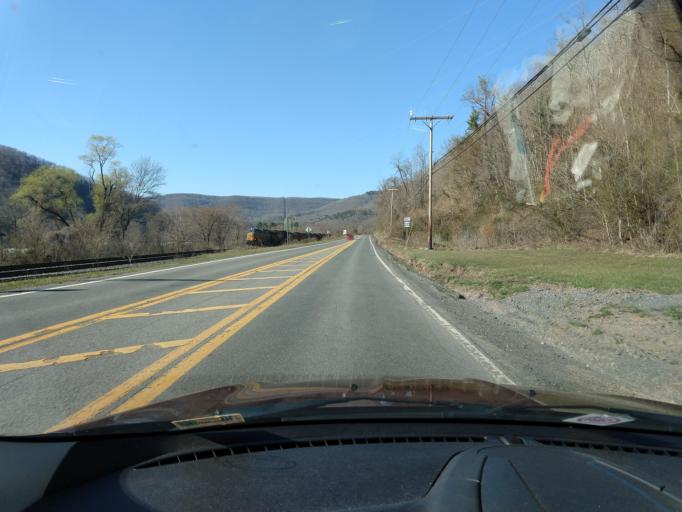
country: US
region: West Virginia
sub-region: Summers County
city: Hinton
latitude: 37.7087
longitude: -80.8875
